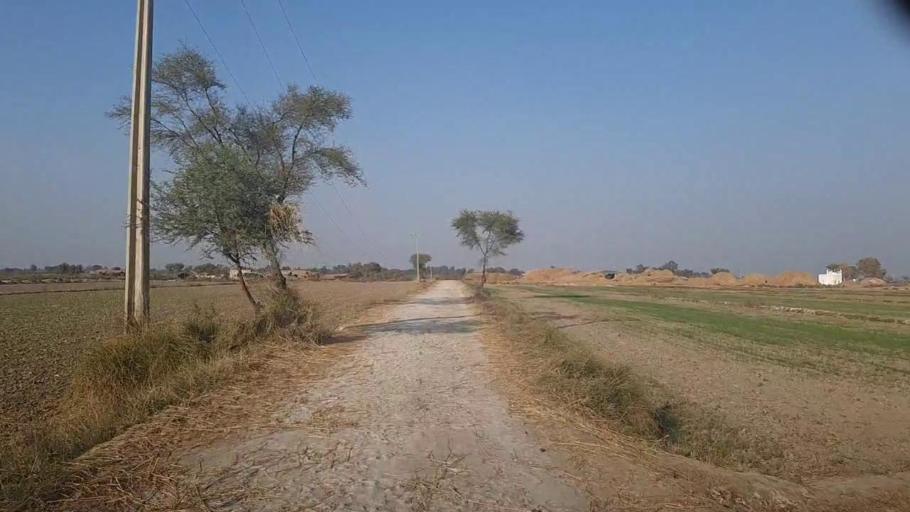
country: PK
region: Sindh
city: Thul
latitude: 28.1643
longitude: 68.8154
